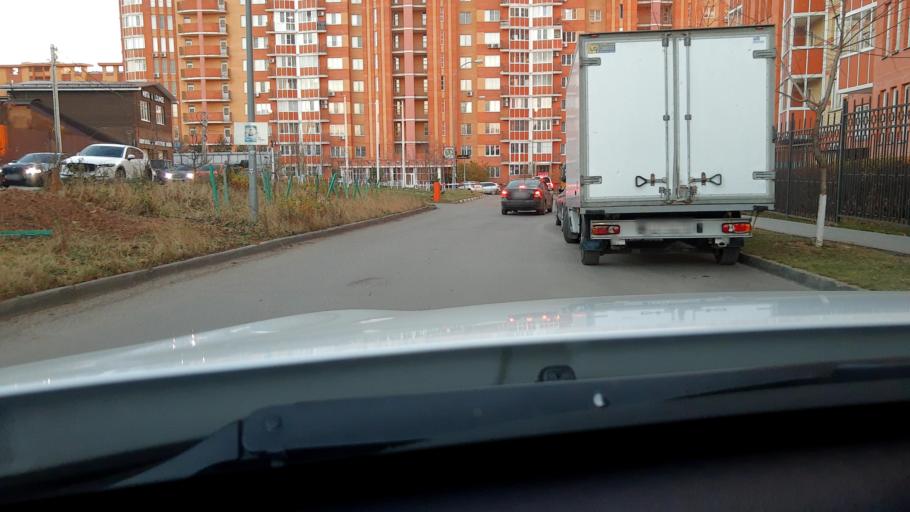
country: RU
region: Moskovskaya
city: Lesnoy Gorodok
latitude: 55.6603
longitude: 37.2298
